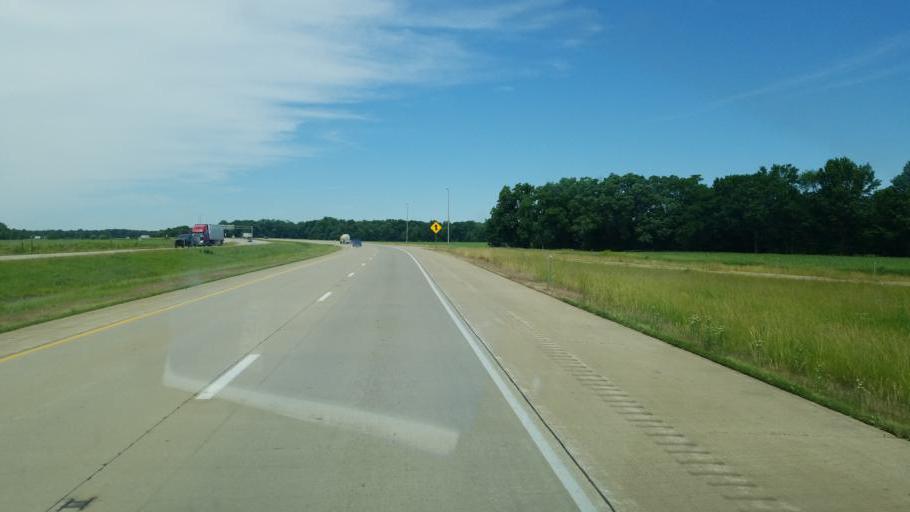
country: US
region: Indiana
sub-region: Vigo County
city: West Terre Haute
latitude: 39.4281
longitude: -87.5611
